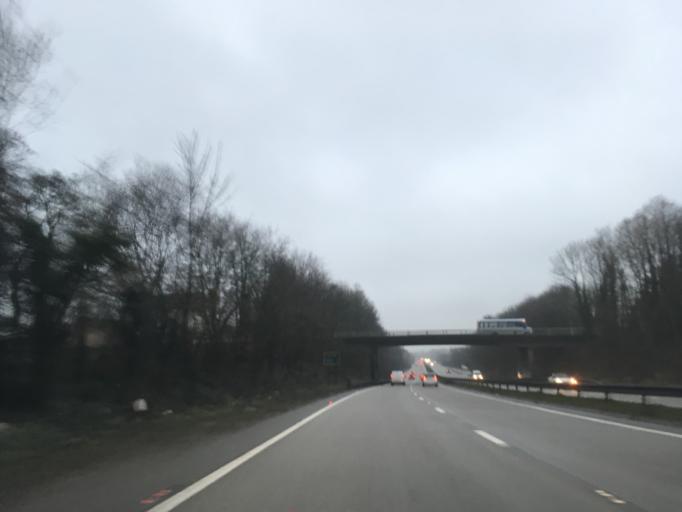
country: GB
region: Wales
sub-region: Cardiff
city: Radyr
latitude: 51.4726
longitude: -3.2791
